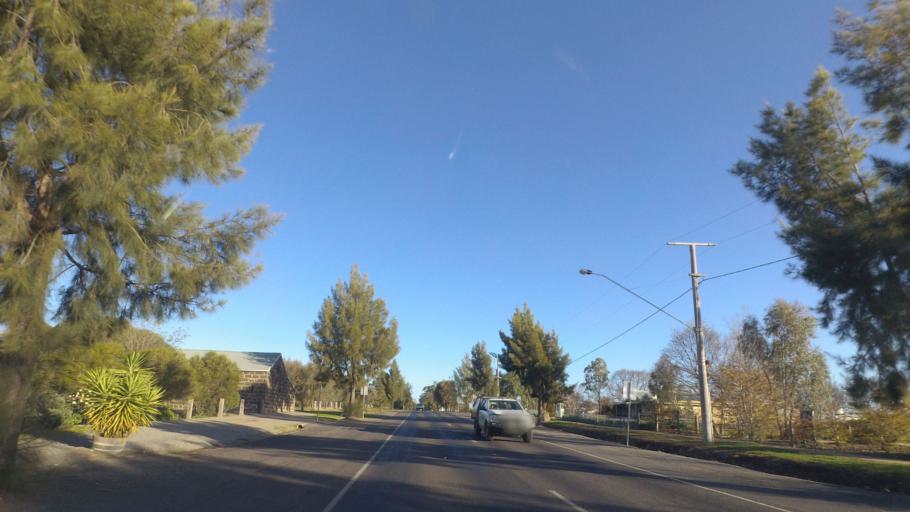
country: AU
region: Victoria
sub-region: Mount Alexander
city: Castlemaine
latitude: -37.0223
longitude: 144.5319
